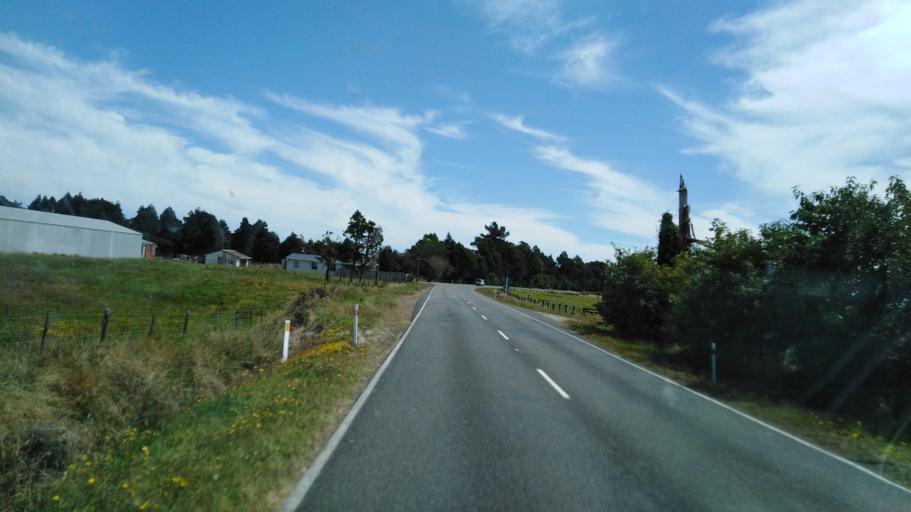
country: NZ
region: West Coast
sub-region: Buller District
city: Westport
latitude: -41.7568
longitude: 171.6369
